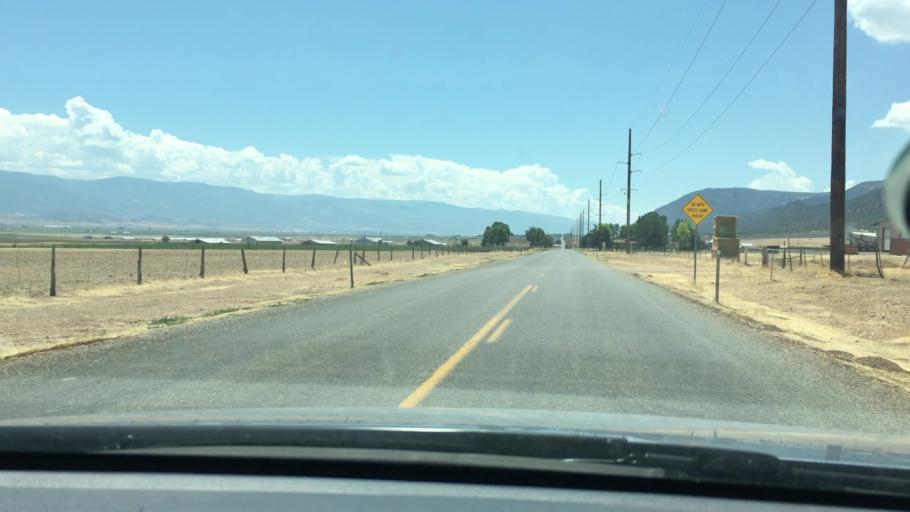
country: US
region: Utah
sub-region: Sanpete County
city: Moroni
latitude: 39.5473
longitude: -111.6401
